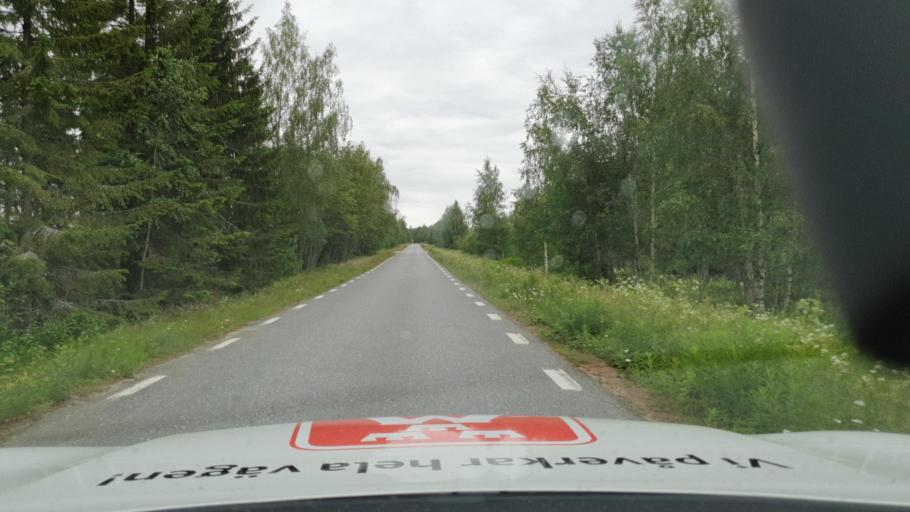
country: SE
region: Vaesterbotten
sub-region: Nordmalings Kommun
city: Nordmaling
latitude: 63.4648
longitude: 19.4652
